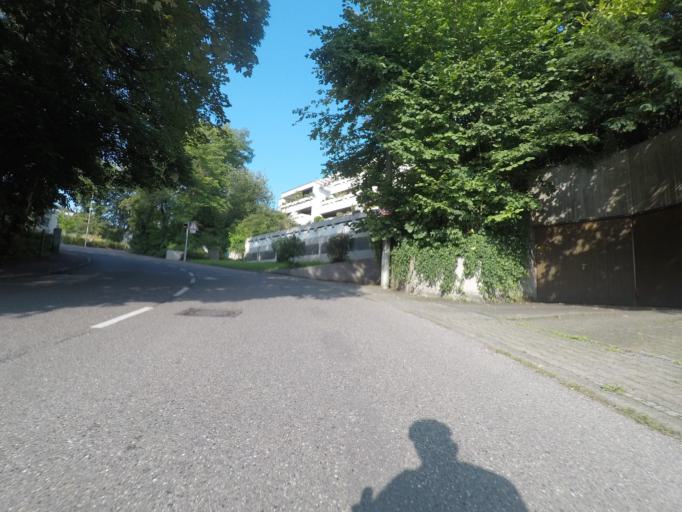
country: DE
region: Baden-Wuerttemberg
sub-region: Regierungsbezirk Stuttgart
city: Stuttgart
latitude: 48.7468
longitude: 9.1217
